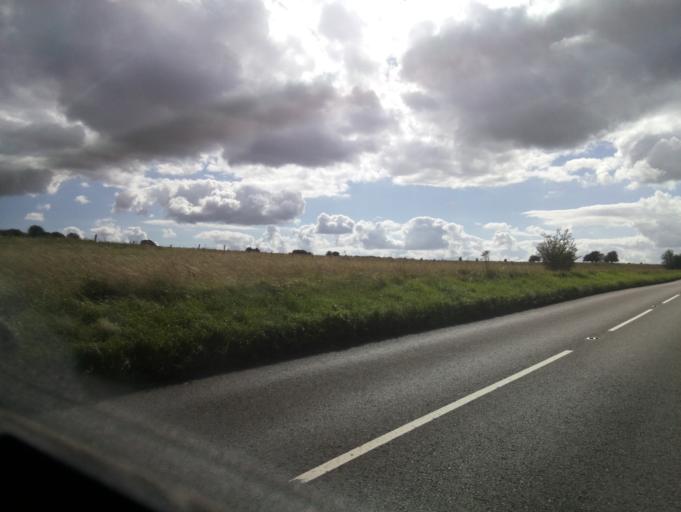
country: GB
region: England
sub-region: Wiltshire
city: Shrewton
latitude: 51.1934
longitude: -1.9457
